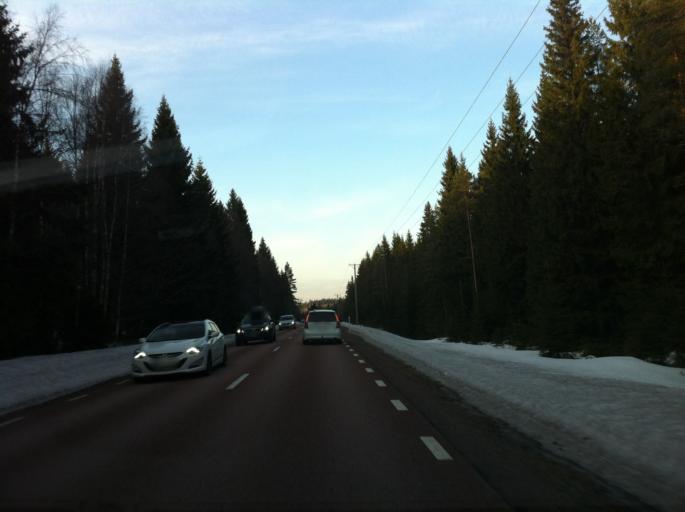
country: SE
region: Vaermland
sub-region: Filipstads Kommun
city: Lesjofors
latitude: 60.2126
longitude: 14.1875
